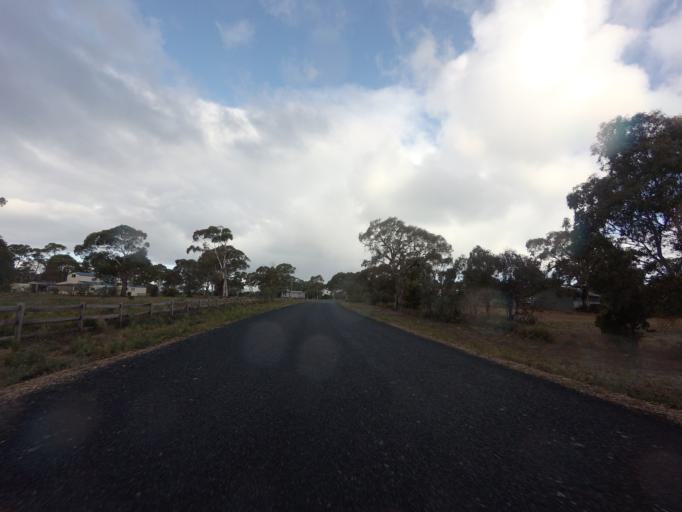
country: AU
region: Tasmania
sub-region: Break O'Day
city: St Helens
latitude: -42.1025
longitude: 148.0777
